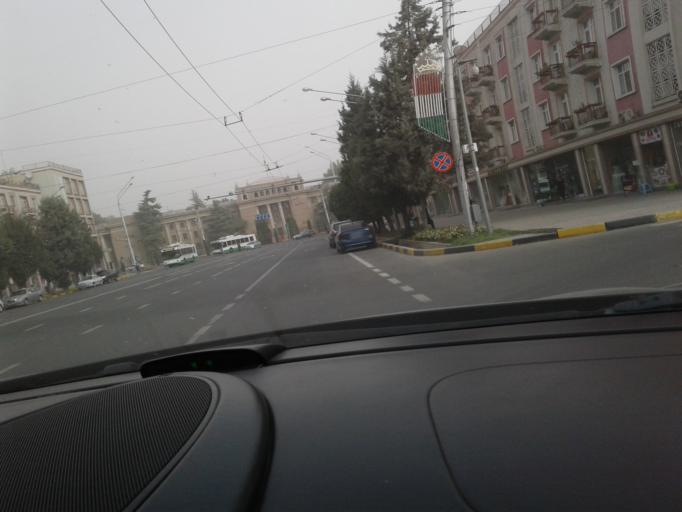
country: TJ
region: Dushanbe
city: Dushanbe
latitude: 38.5830
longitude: 68.7852
